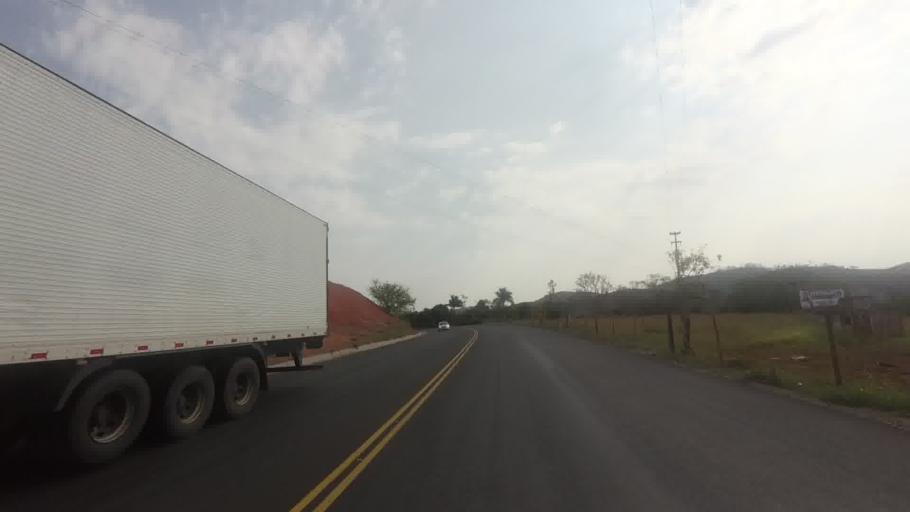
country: BR
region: Rio de Janeiro
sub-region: Itaperuna
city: Itaperuna
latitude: -21.2603
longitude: -41.7700
